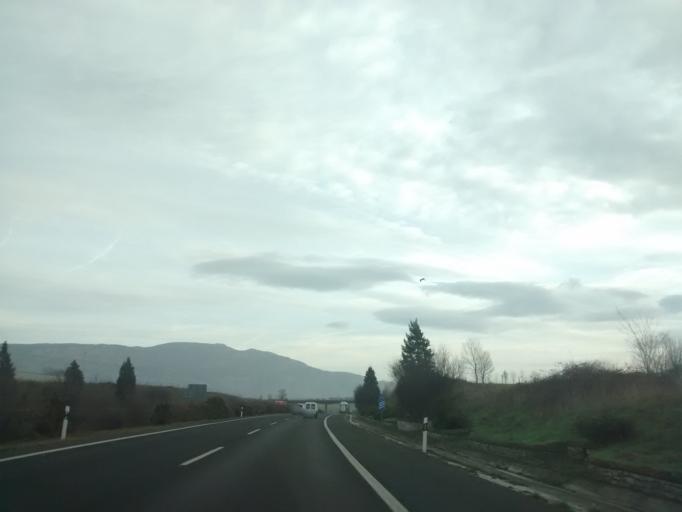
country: ES
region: Navarre
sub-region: Provincia de Navarra
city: Arbizu
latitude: 42.9061
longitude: -2.0464
